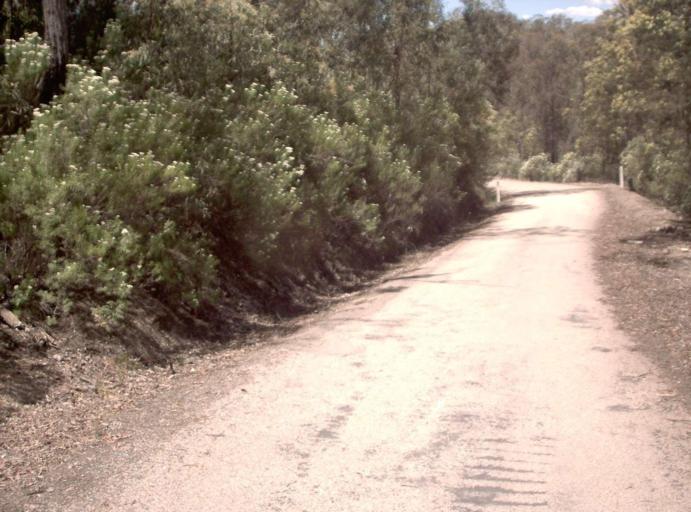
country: AU
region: New South Wales
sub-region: Snowy River
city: Jindabyne
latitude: -37.0773
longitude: 148.3428
